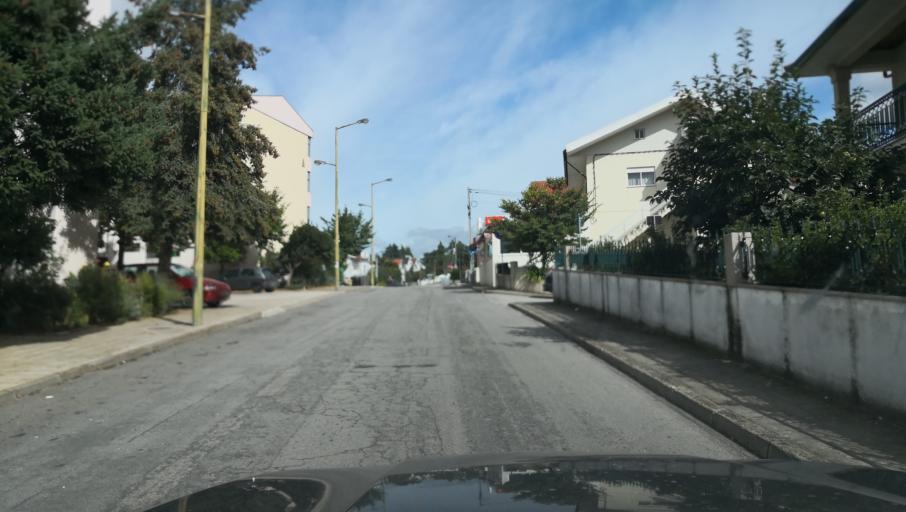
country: PT
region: Vila Real
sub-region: Vila Real
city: Vila Real
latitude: 41.2935
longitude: -7.7295
